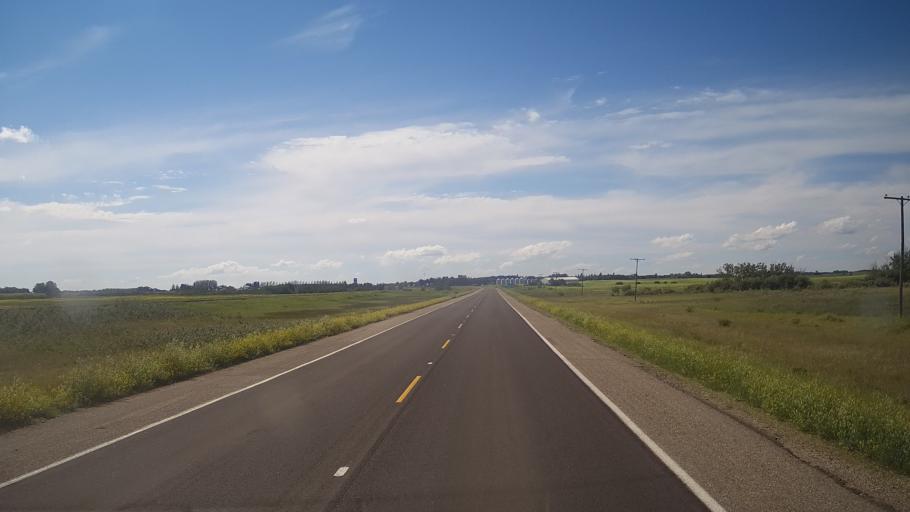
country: CA
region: Saskatchewan
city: Foam Lake
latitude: 51.2537
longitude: -103.7104
